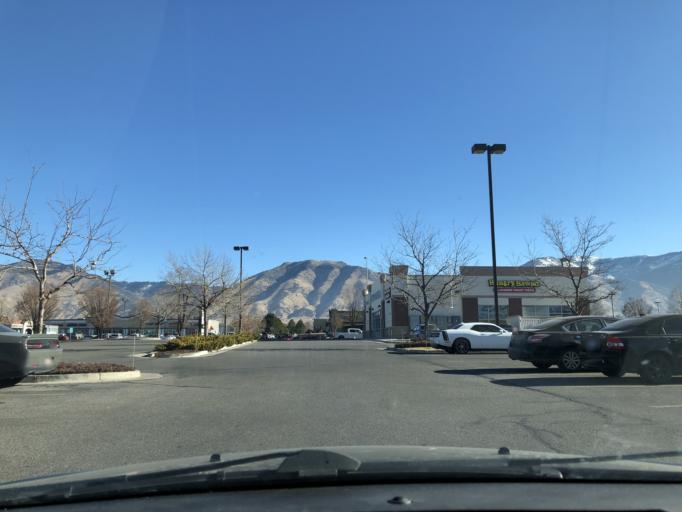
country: US
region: Utah
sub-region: Cache County
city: Logan
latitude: 41.7594
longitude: -111.8355
